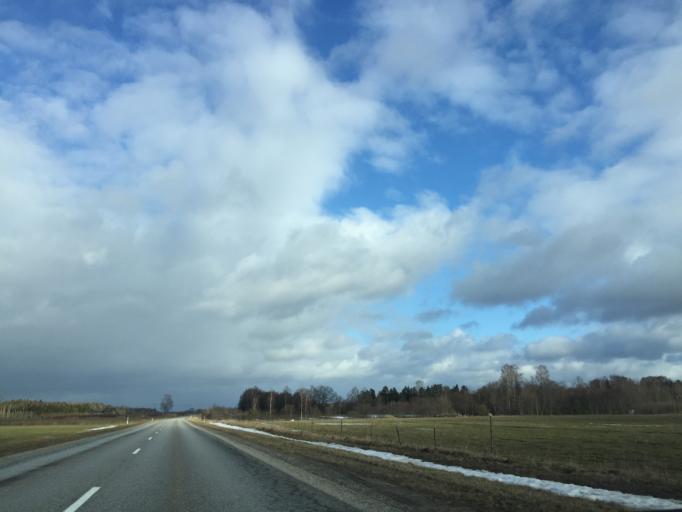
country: LV
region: Aloja
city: Staicele
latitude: 57.8744
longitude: 24.5796
